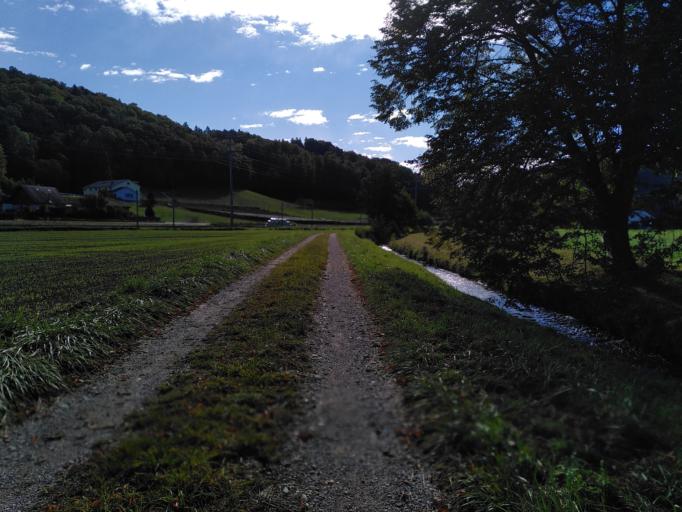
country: CH
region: Bern
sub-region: Oberaargau
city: Seeberg
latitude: 47.1478
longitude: 7.6945
